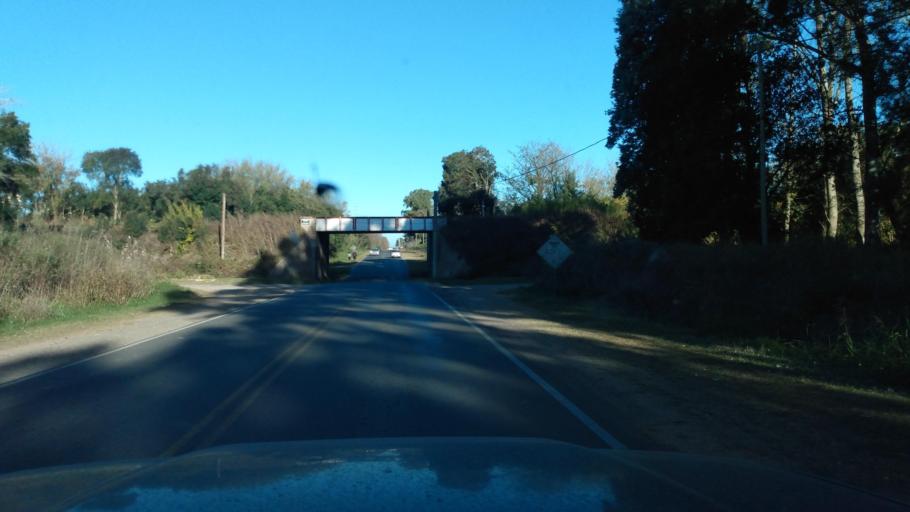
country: AR
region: Buenos Aires
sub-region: Partido de Lujan
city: Lujan
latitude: -34.5336
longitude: -59.1656
